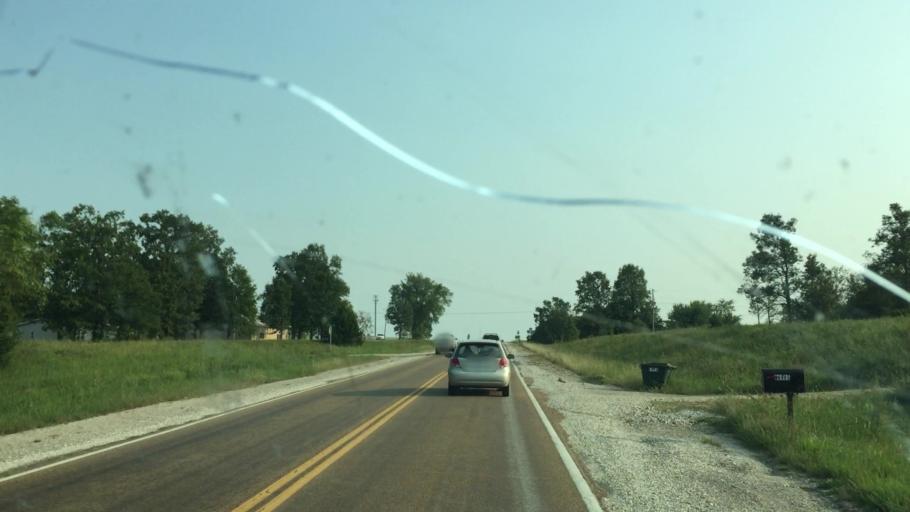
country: US
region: Missouri
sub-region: Pulaski County
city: Richland
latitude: 37.7736
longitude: -92.4078
